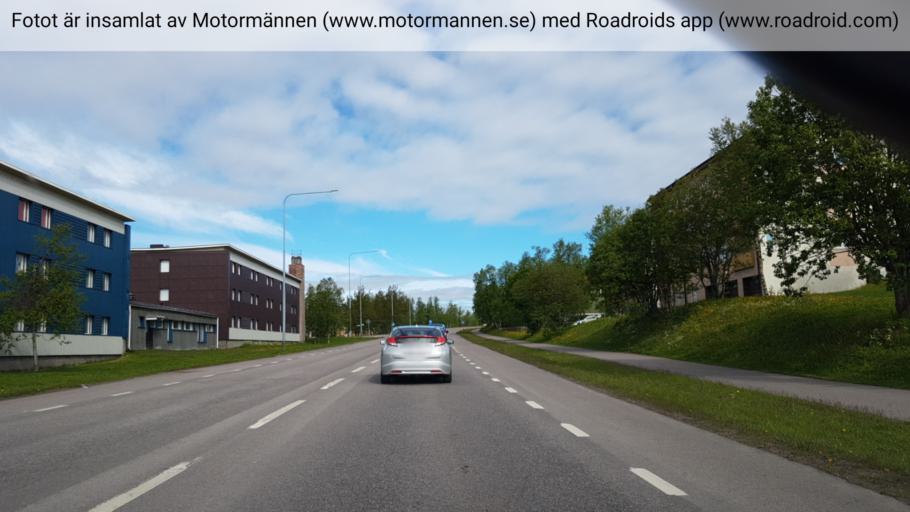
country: SE
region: Norrbotten
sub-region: Kiruna Kommun
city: Kiruna
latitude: 67.8479
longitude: 20.2285
